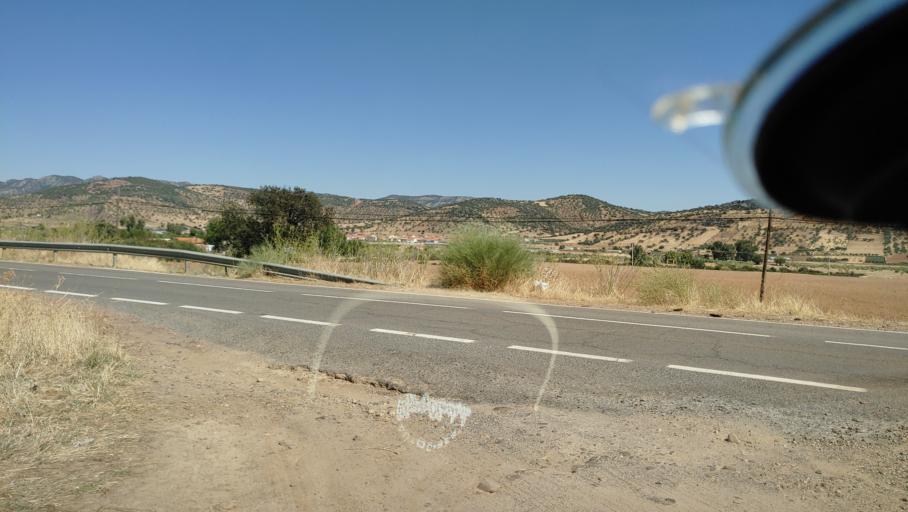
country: ES
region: Castille-La Mancha
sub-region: Provincia de Ciudad Real
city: Guadalmez
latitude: 38.7130
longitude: -4.9700
